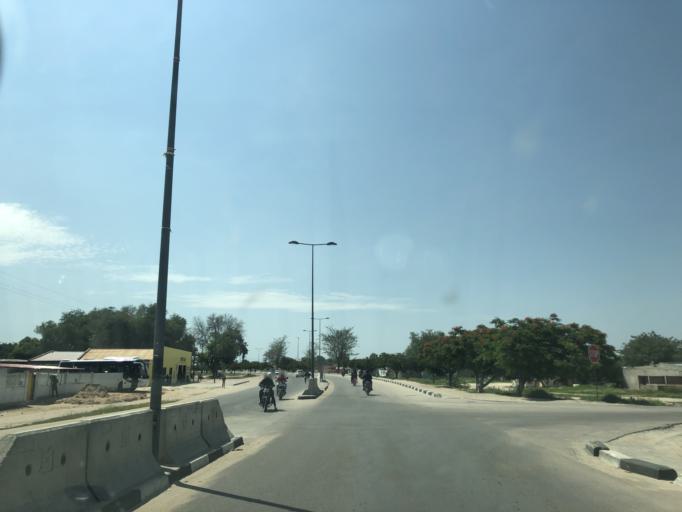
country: AO
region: Cunene
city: Ondjiva
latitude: -17.0685
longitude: 15.7100
